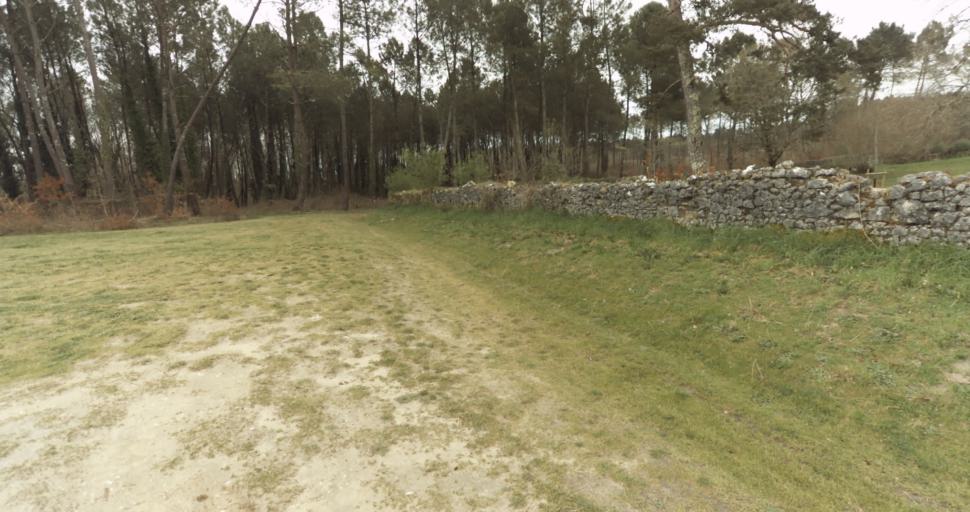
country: FR
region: Aquitaine
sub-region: Departement des Landes
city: Roquefort
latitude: 44.0398
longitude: -0.3094
